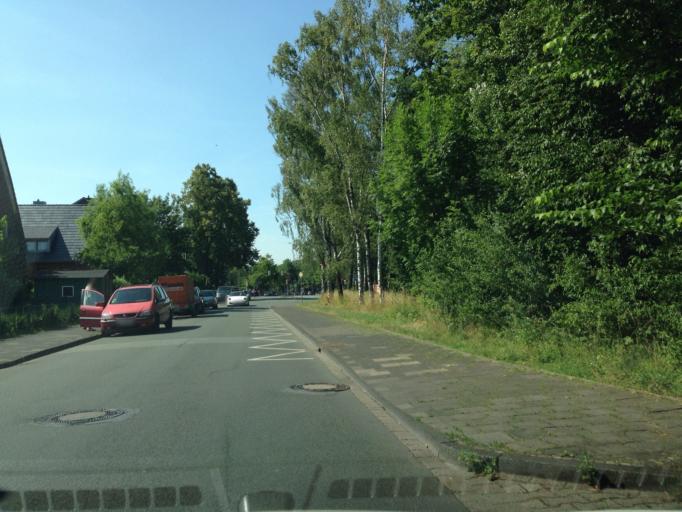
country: DE
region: North Rhine-Westphalia
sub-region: Regierungsbezirk Munster
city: Muenster
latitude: 51.9718
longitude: 7.5677
